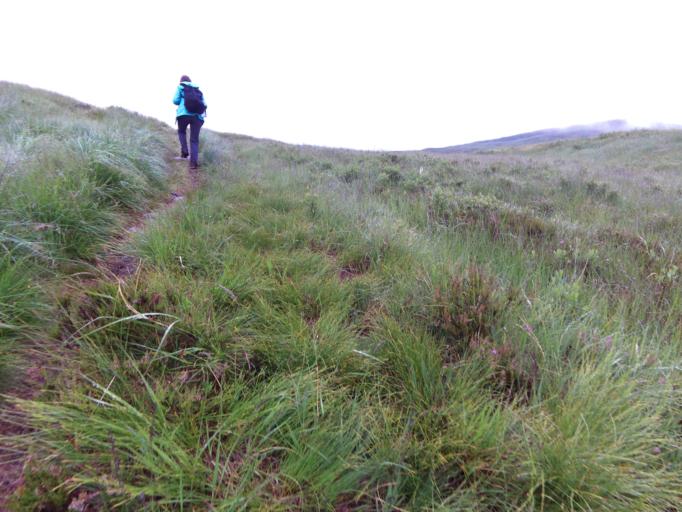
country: GB
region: Scotland
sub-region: Highland
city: Spean Bridge
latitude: 56.7715
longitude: -4.7099
